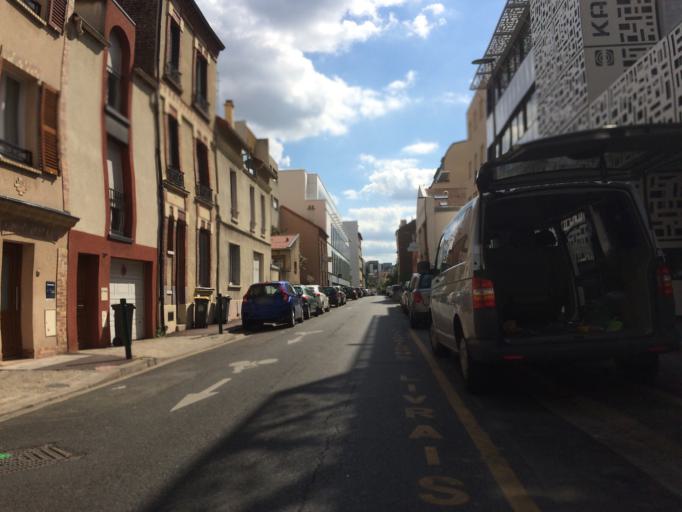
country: FR
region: Ile-de-France
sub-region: Departement des Hauts-de-Seine
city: Suresnes
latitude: 48.8754
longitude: 2.2269
